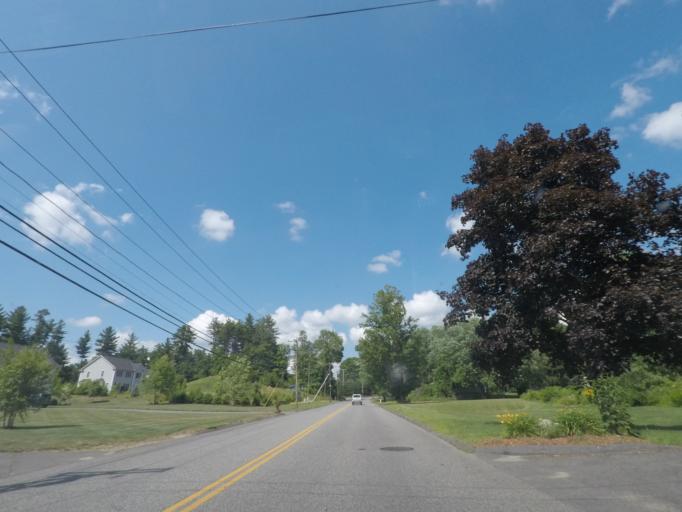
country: US
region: Massachusetts
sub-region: Hampden County
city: Monson
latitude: 42.1104
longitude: -72.3109
